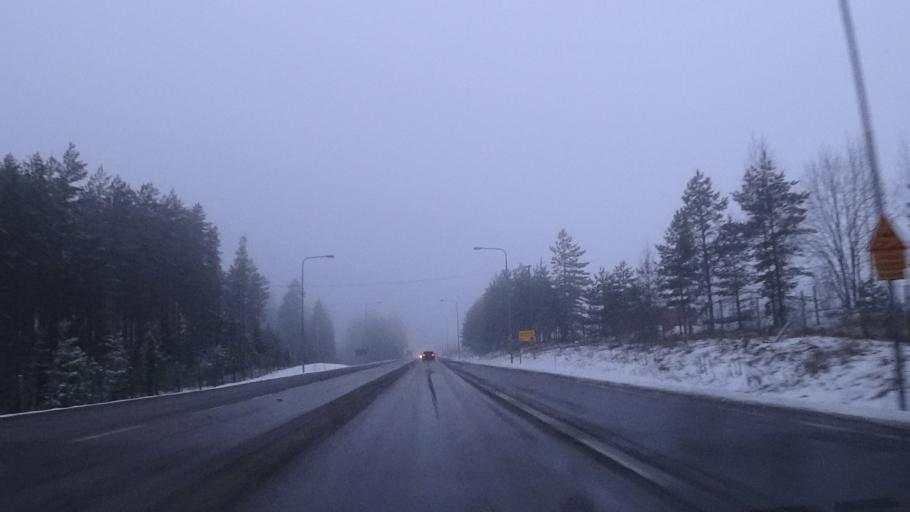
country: FI
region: Paijanne Tavastia
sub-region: Lahti
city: Hollola
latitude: 60.9848
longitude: 25.4107
